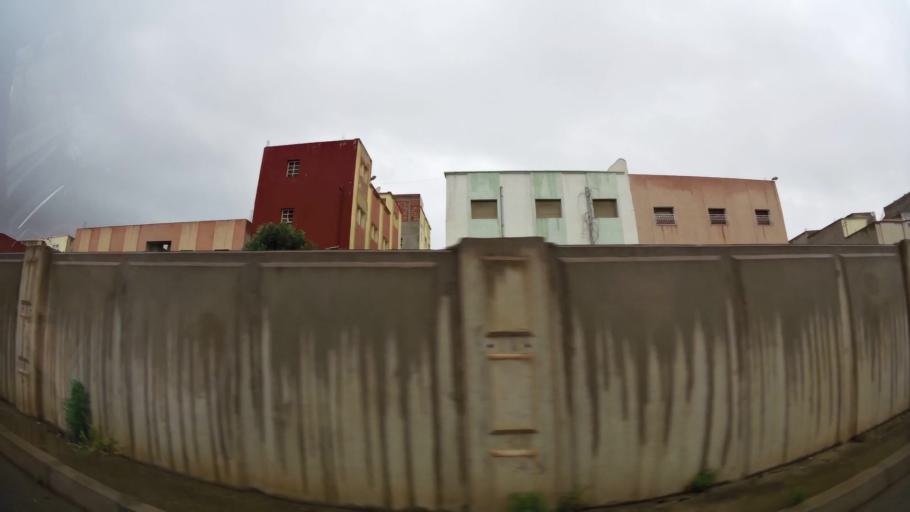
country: MA
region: Oriental
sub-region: Nador
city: Nador
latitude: 35.1556
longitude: -2.9744
